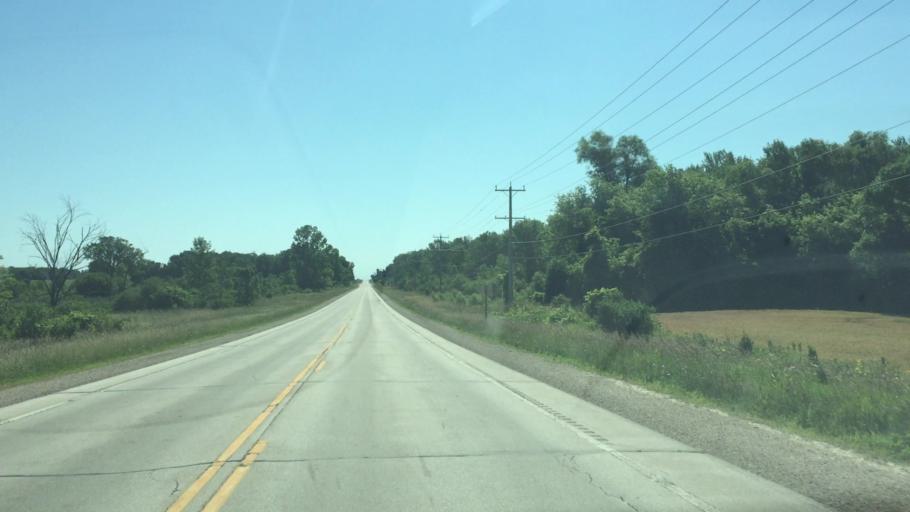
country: US
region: Wisconsin
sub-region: Calumet County
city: Sherwood
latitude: 44.1409
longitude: -88.2551
